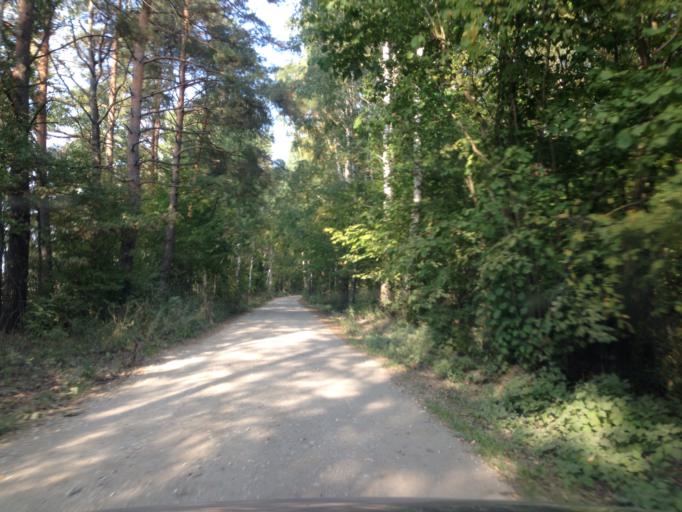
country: PL
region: Kujawsko-Pomorskie
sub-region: Powiat brodnicki
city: Gorzno
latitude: 53.2164
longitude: 19.6401
